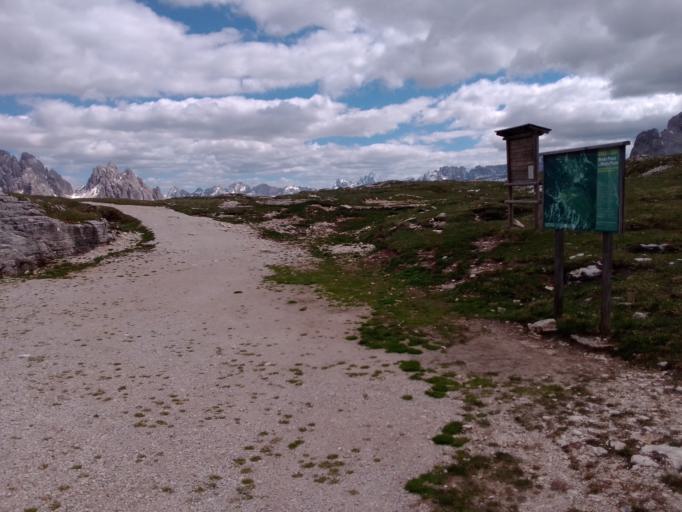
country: IT
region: Trentino-Alto Adige
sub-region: Bolzano
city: Dobbiaco
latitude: 46.6163
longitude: 12.2430
